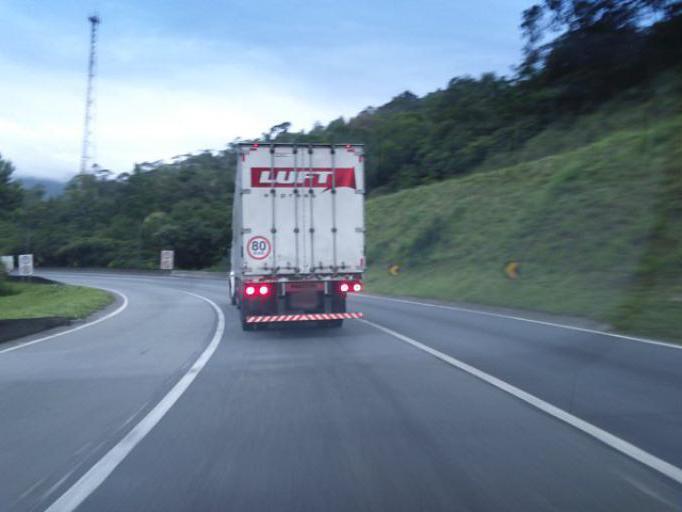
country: BR
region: Parana
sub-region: Guaratuba
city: Guaratuba
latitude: -25.8666
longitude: -48.9483
